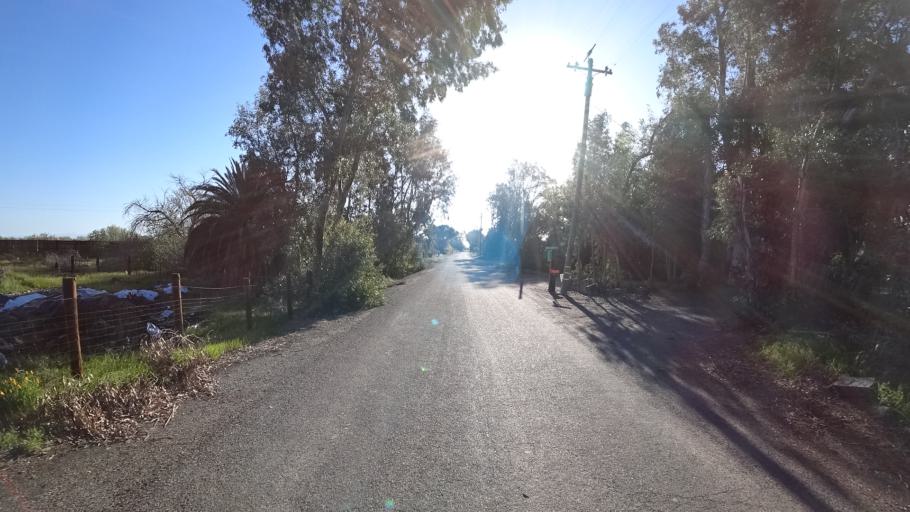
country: US
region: California
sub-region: Glenn County
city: Orland
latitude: 39.7696
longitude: -122.2262
